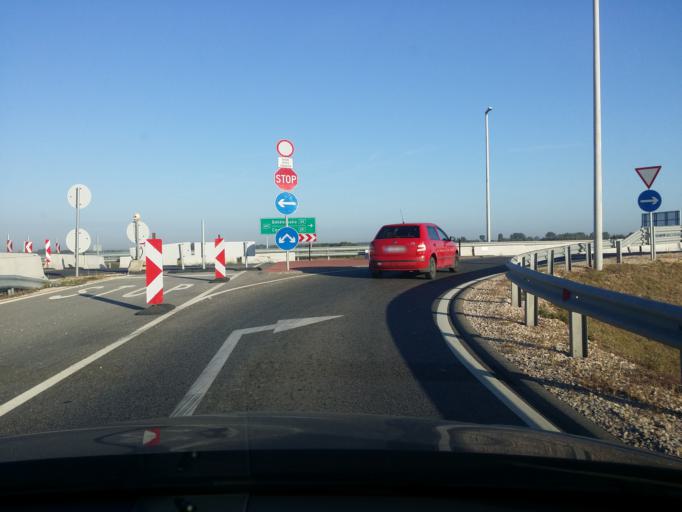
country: HU
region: Bacs-Kiskun
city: Kecskemet
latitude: 46.9398
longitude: 19.6579
